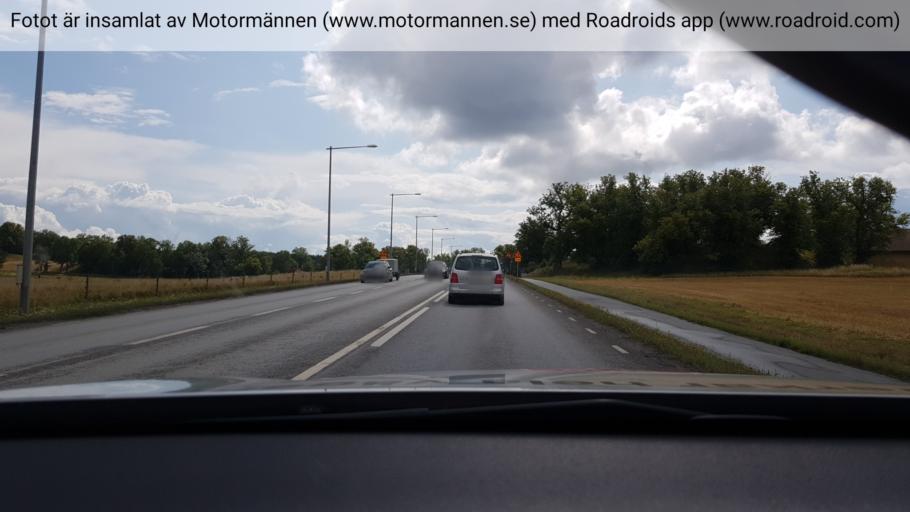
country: SE
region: Stockholm
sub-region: Ekero Kommun
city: Ekeroe
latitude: 59.3235
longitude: 17.8688
